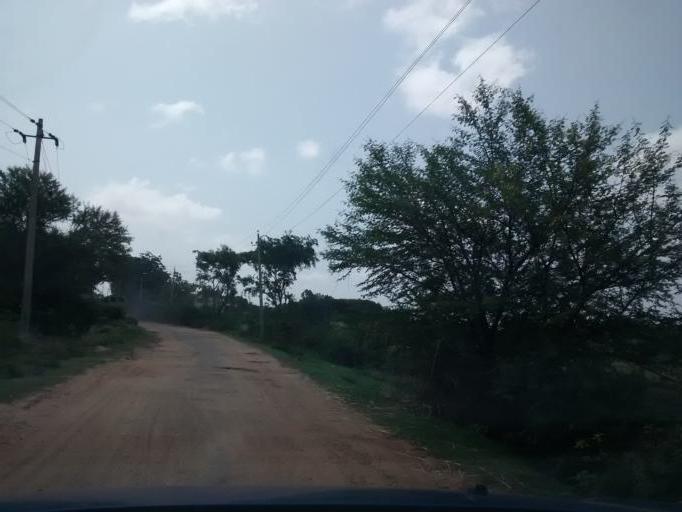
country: IN
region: Karnataka
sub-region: Hassan
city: Hole Narsipur
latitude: 12.6926
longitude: 76.1840
